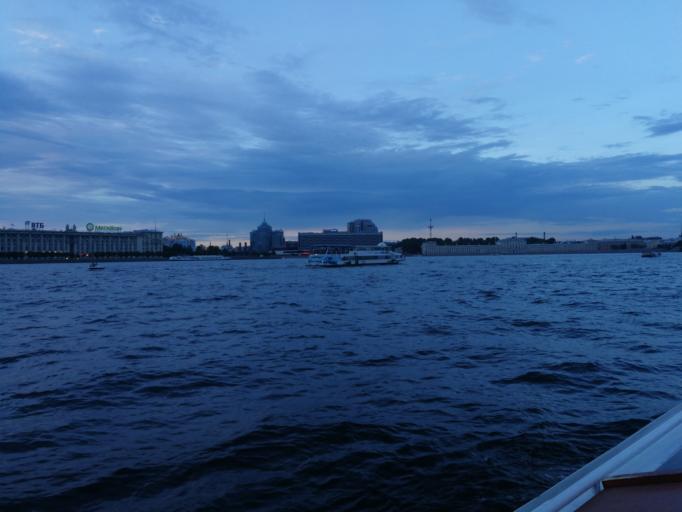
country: RU
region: St.-Petersburg
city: Saint Petersburg
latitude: 59.9485
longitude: 30.3337
